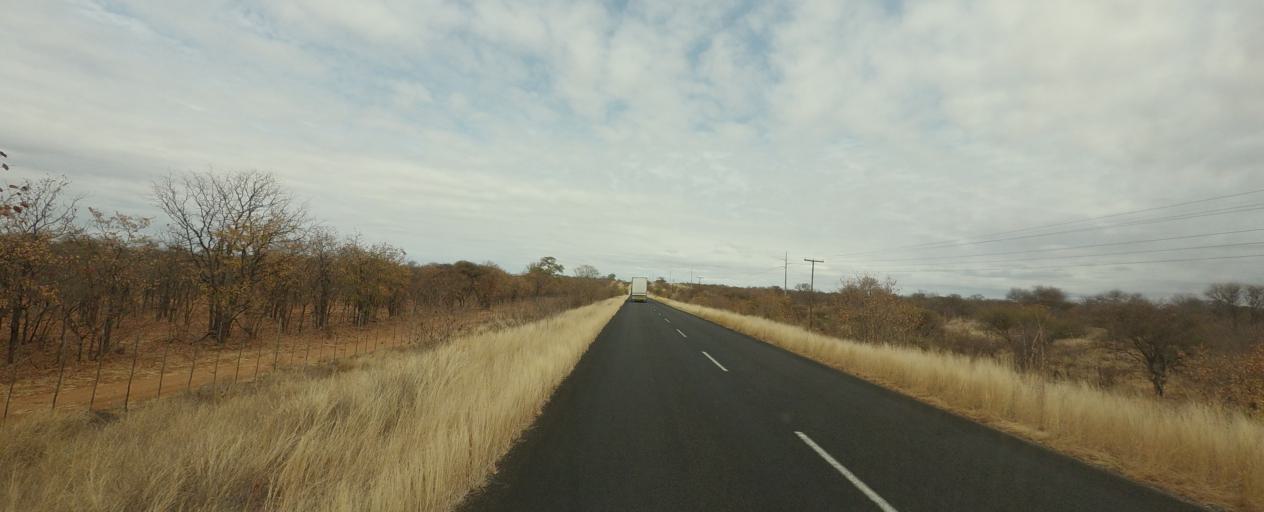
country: ZW
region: Matabeleland South
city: Beitbridge
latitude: -22.4299
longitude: 29.4321
